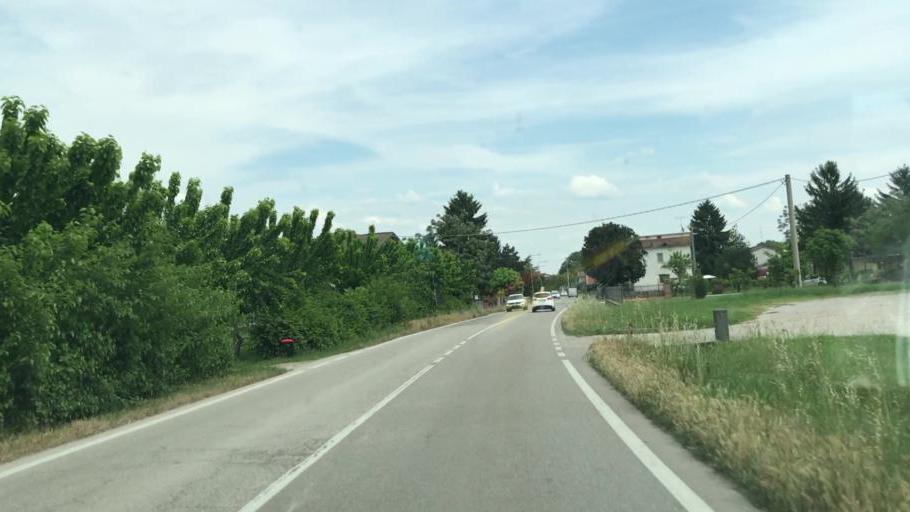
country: IT
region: Lombardy
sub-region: Provincia di Mantova
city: Bagnolo San Vito
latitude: 45.1206
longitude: 10.8988
